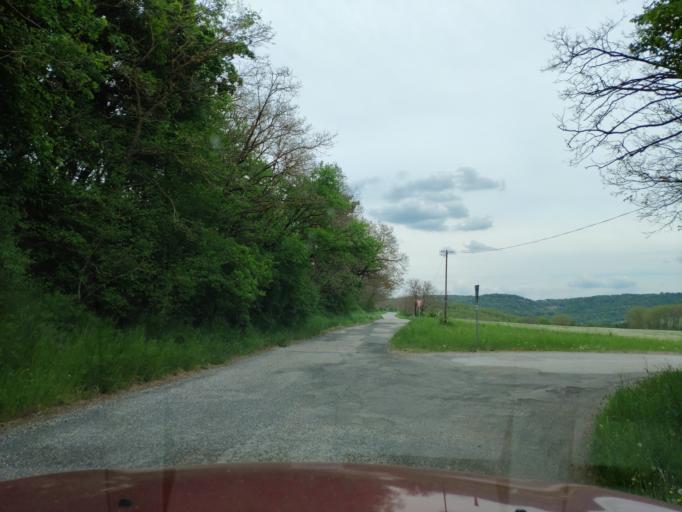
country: SK
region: Banskobystricky
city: Rimavska Sobota
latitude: 48.4874
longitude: 20.0941
